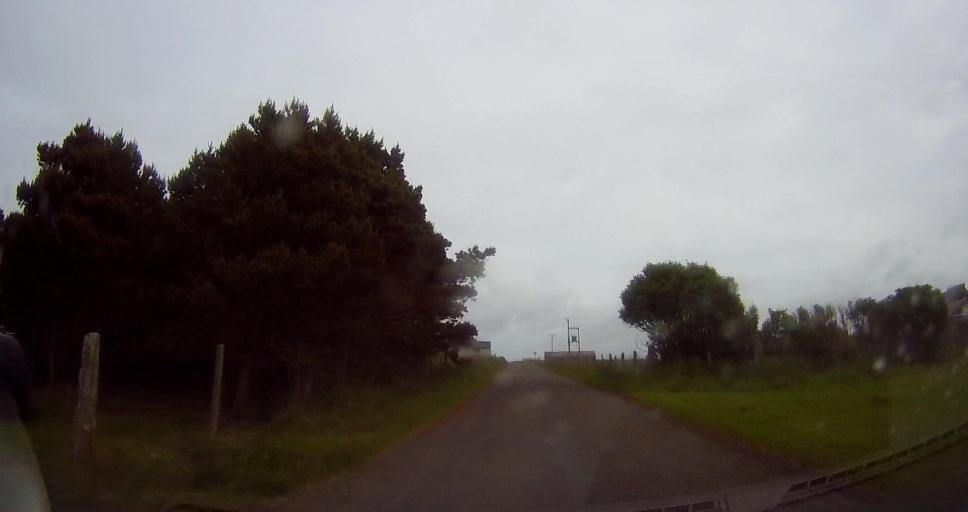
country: GB
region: Scotland
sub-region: Orkney Islands
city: Stromness
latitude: 58.8322
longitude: -3.2066
